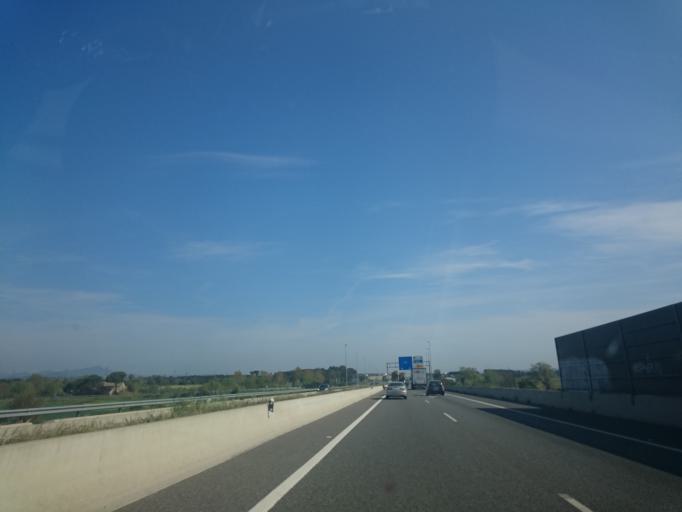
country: ES
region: Catalonia
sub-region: Provincia de Girona
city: Riudellots de la Selva
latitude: 41.8817
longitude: 2.7811
